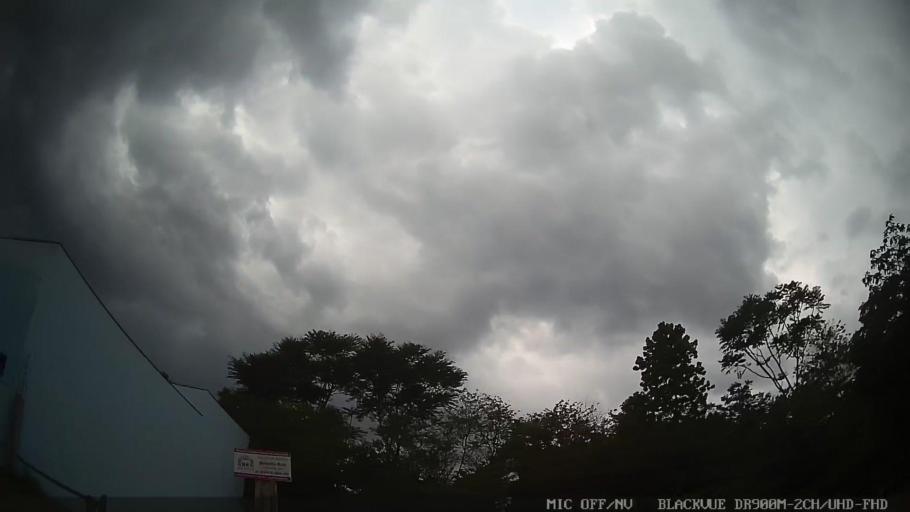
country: BR
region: Sao Paulo
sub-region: Itatiba
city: Itatiba
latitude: -23.0078
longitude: -46.8590
